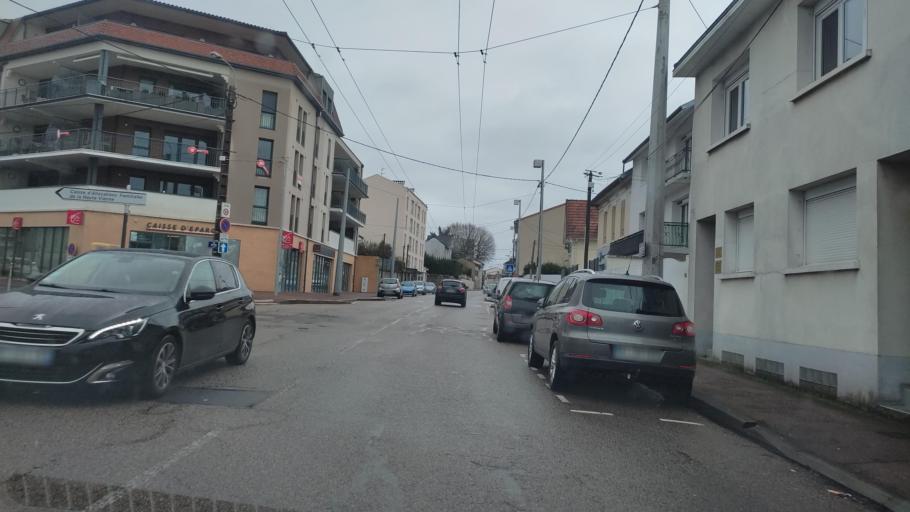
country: FR
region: Limousin
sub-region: Departement de la Haute-Vienne
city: Isle
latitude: 45.8247
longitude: 1.2285
